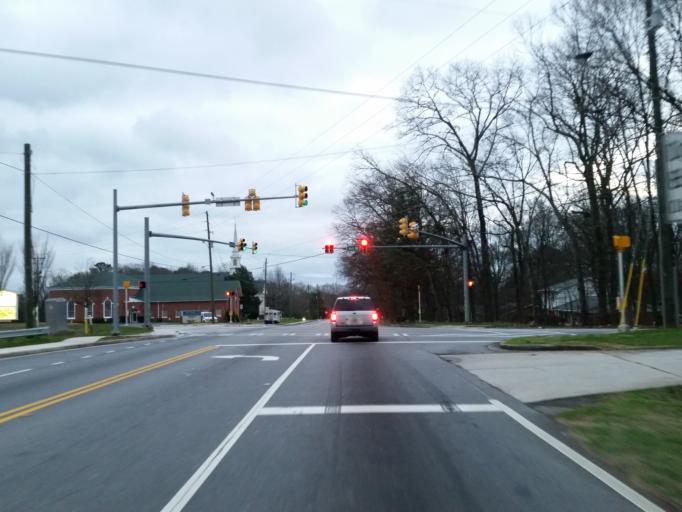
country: US
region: Georgia
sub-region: Cobb County
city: Mableton
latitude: 33.8653
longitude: -84.5772
